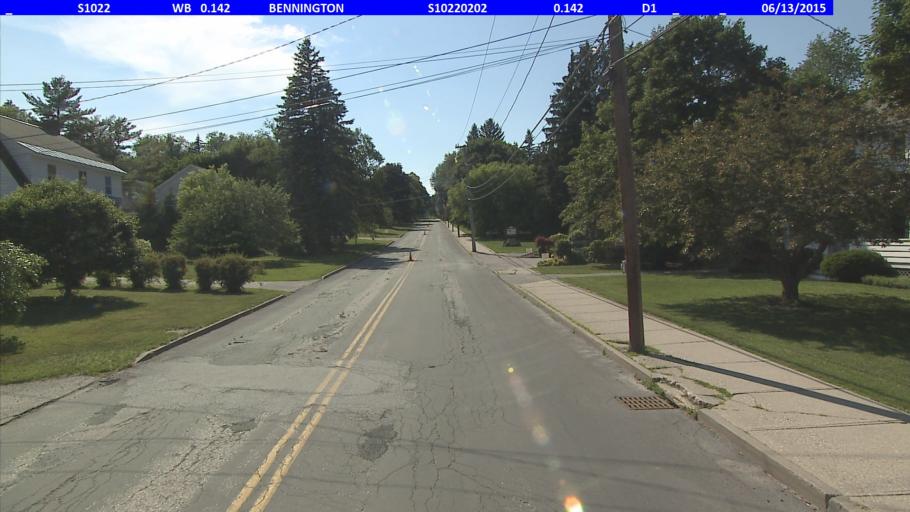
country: US
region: Vermont
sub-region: Bennington County
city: Bennington
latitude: 42.8782
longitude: -73.2070
